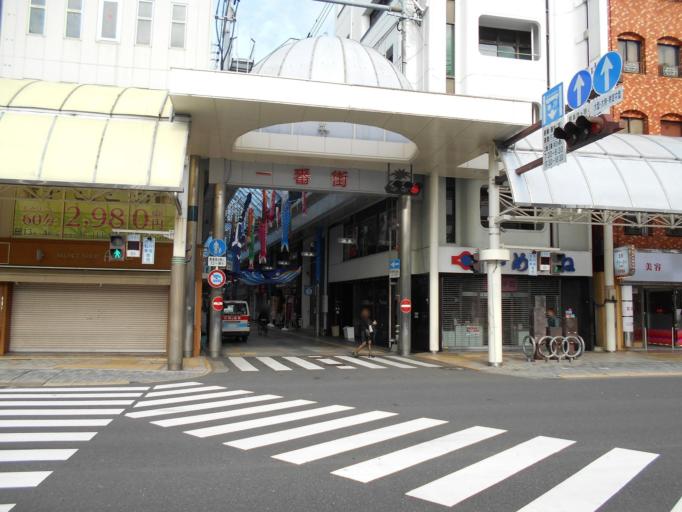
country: JP
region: Miyazaki
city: Miyazaki-shi
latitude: 31.9152
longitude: 131.4229
